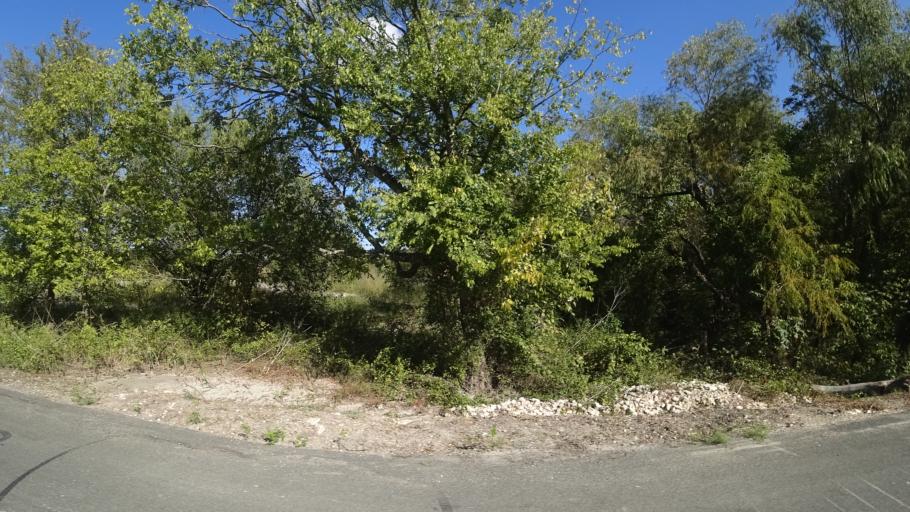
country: US
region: Texas
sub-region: Travis County
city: Manor
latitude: 30.3606
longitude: -97.6062
